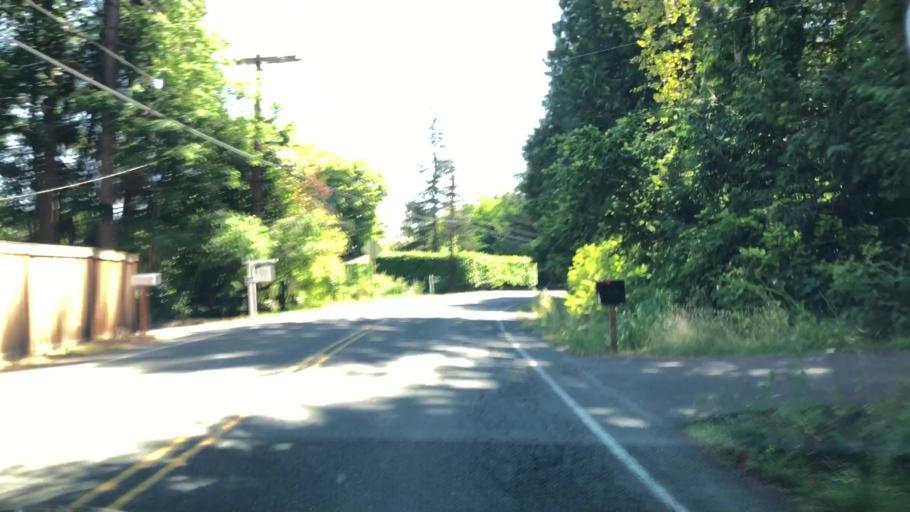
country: US
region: Washington
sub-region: King County
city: Cottage Lake
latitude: 47.7551
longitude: -122.1083
